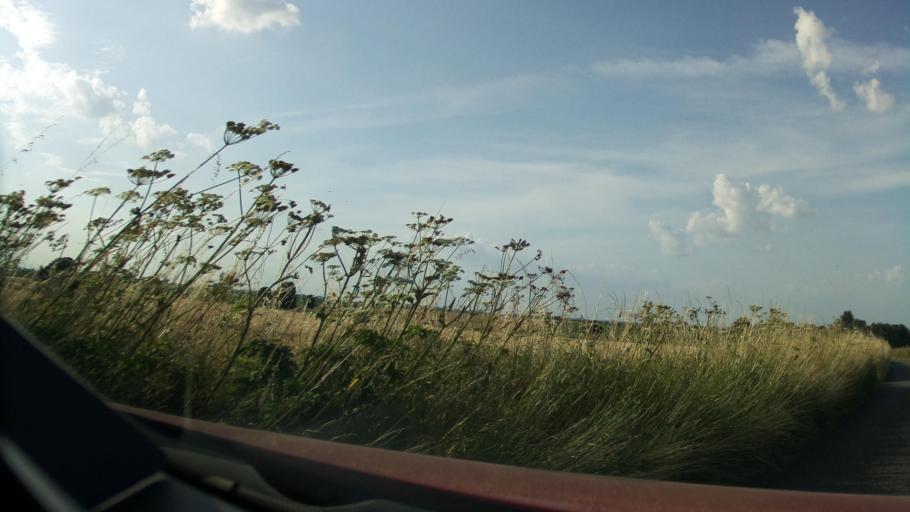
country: GB
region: England
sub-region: South Gloucestershire
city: Marshfield
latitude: 51.4725
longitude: -2.3114
